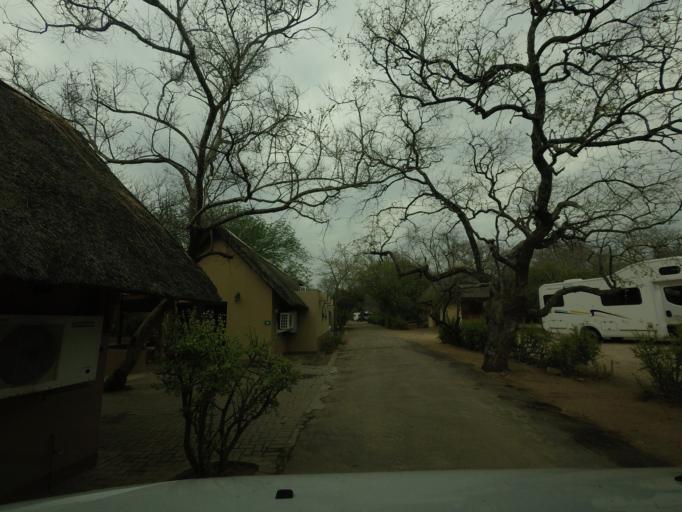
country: ZA
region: Limpopo
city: Thulamahashi
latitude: -24.4746
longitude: 31.3907
